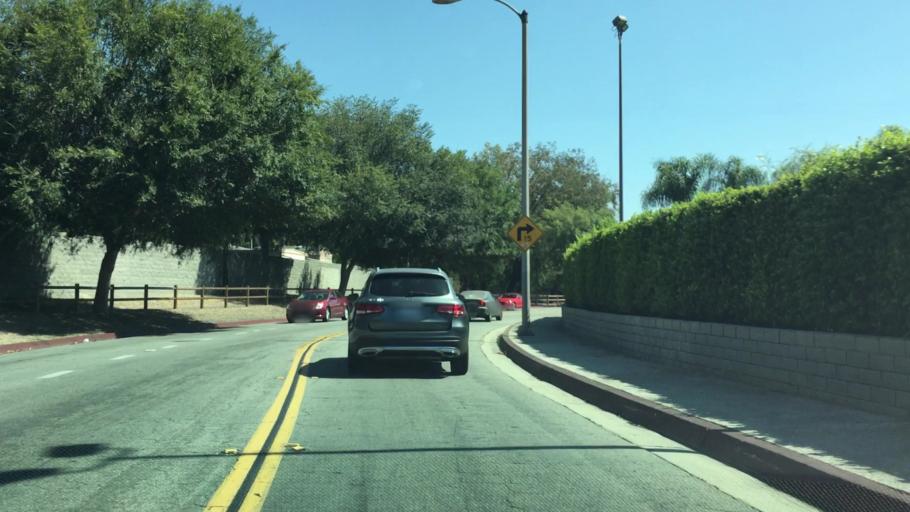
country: US
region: California
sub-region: Los Angeles County
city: Rowland Heights
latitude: 33.9939
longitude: -117.9117
